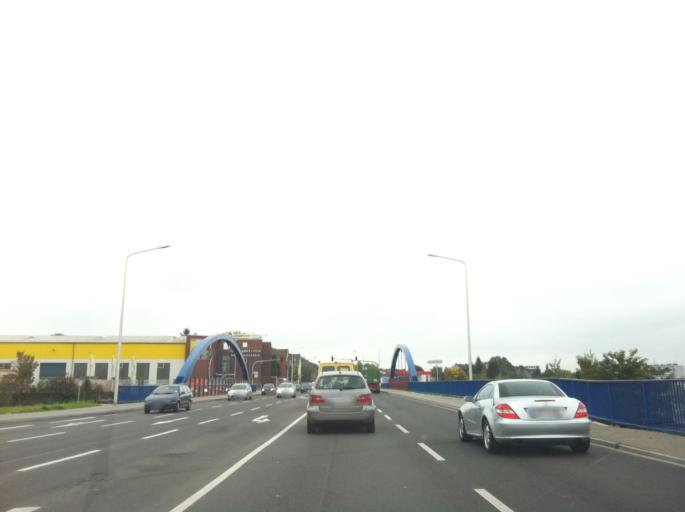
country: DE
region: North Rhine-Westphalia
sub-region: Regierungsbezirk Koln
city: Dueren
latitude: 50.8156
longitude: 6.4878
